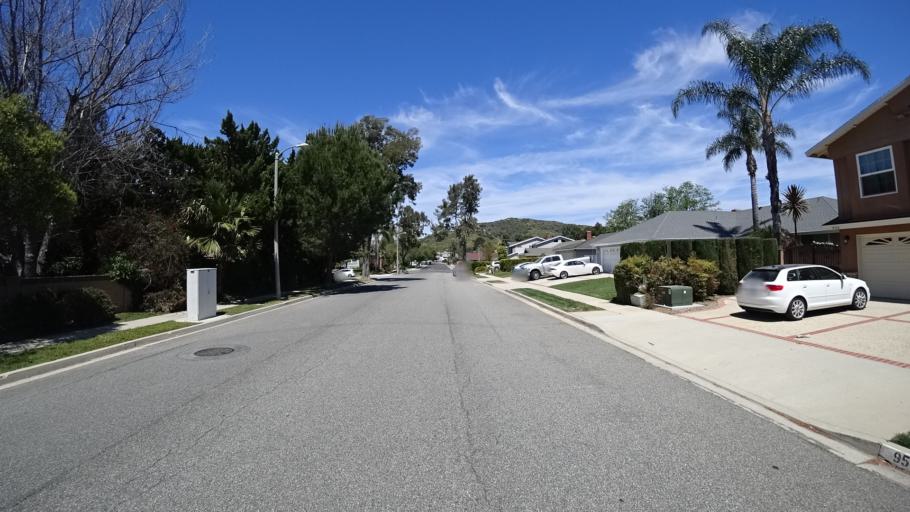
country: US
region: California
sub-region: Ventura County
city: Casa Conejo
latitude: 34.1605
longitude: -118.9549
